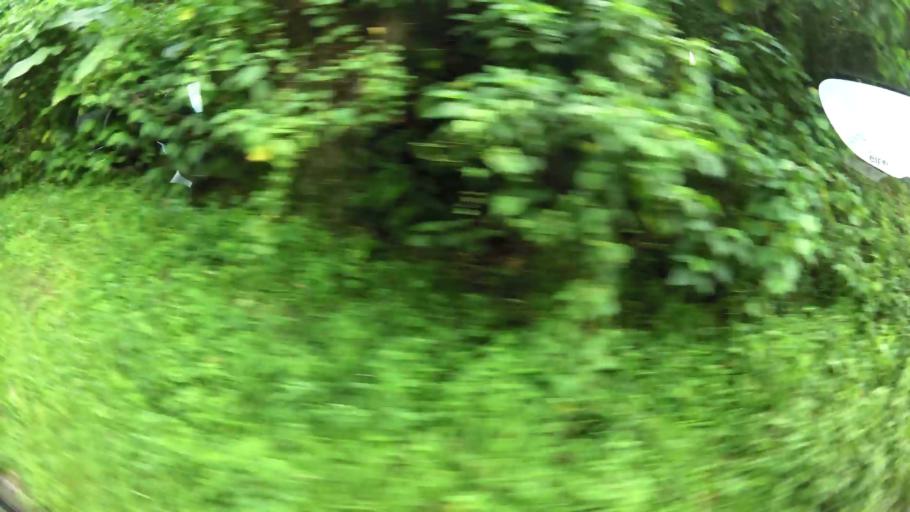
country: MQ
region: Martinique
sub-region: Martinique
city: Le Morne-Rouge
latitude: 14.7624
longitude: -61.1579
